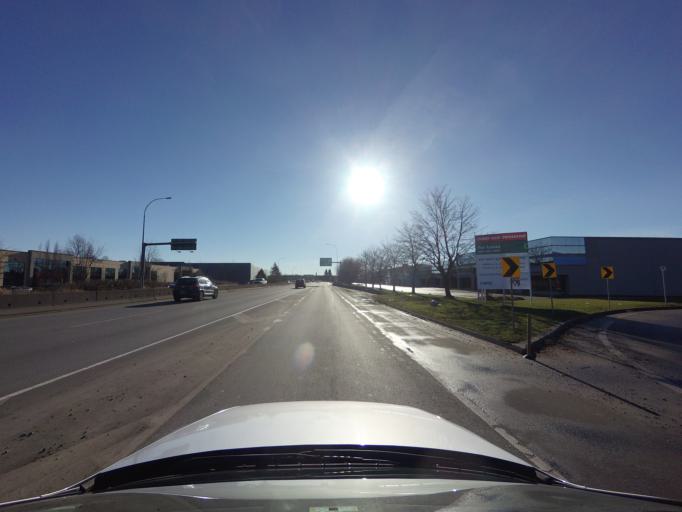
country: CA
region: British Columbia
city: Richmond
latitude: 49.1878
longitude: -123.0779
